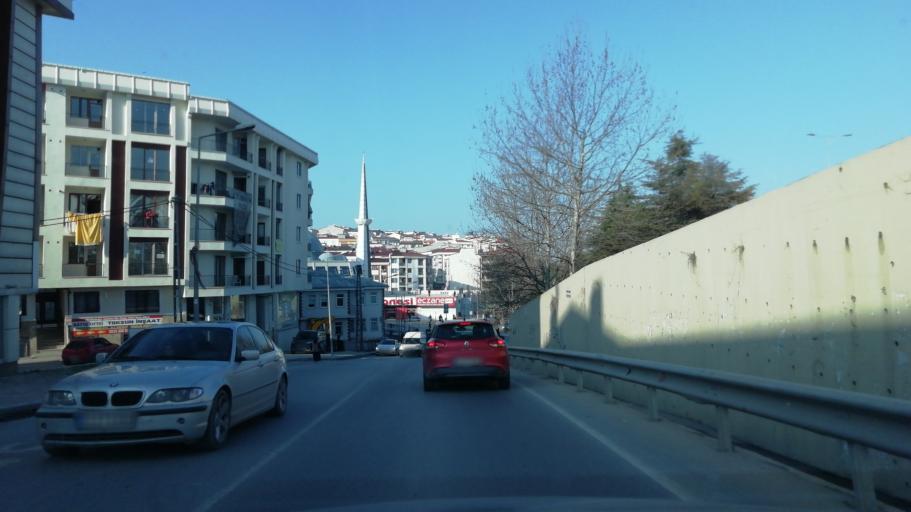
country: TR
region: Istanbul
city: Esenyurt
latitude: 41.0391
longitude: 28.6887
